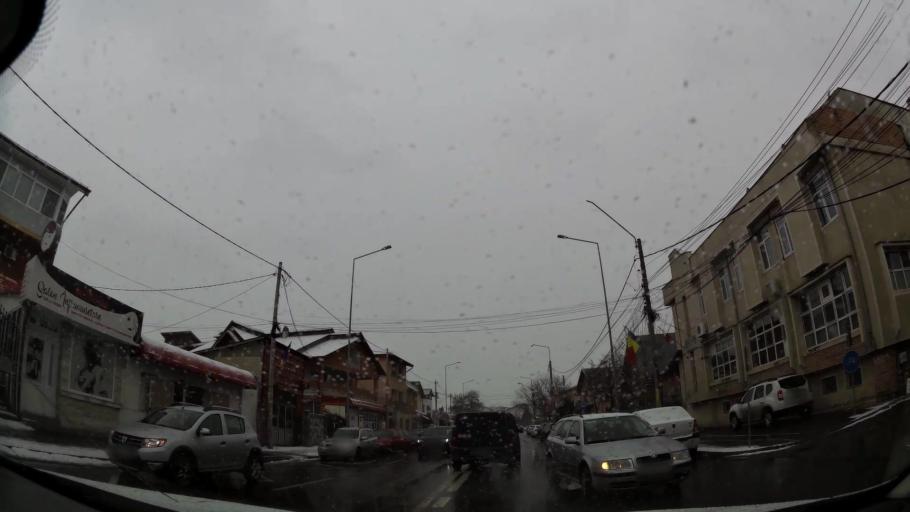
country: RO
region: Dambovita
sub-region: Municipiul Targoviste
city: Targoviste
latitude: 44.9266
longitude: 25.4467
